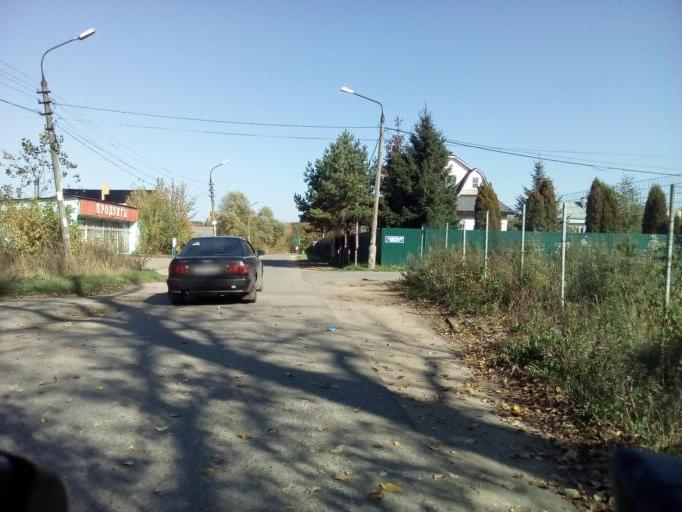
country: RU
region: Moskovskaya
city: Ramenskoye
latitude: 55.5441
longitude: 38.2958
